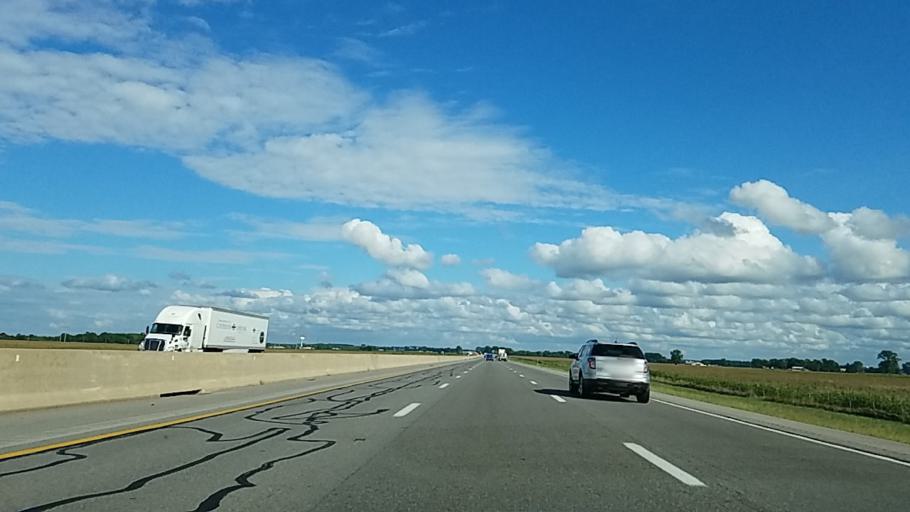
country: US
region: Ohio
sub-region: Erie County
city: Milan
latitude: 41.3321
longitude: -82.6656
